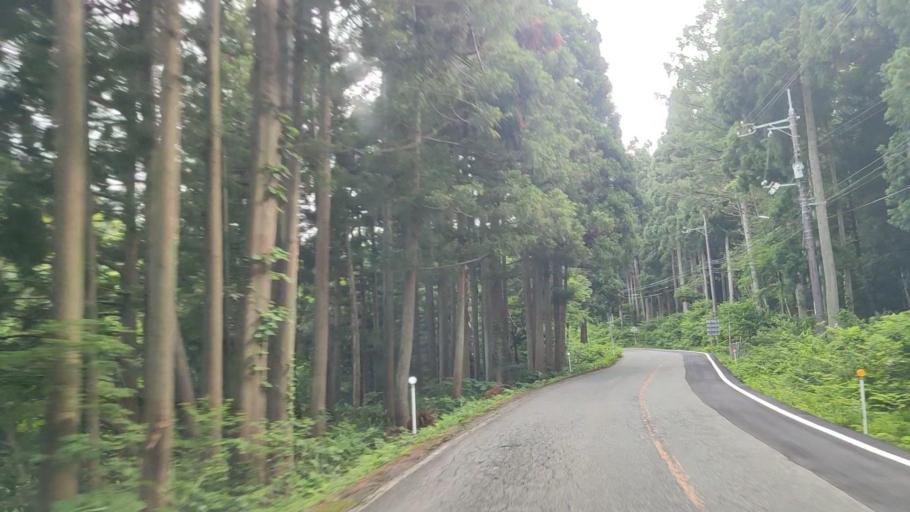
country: JP
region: Tottori
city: Yonago
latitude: 35.3339
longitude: 133.5570
